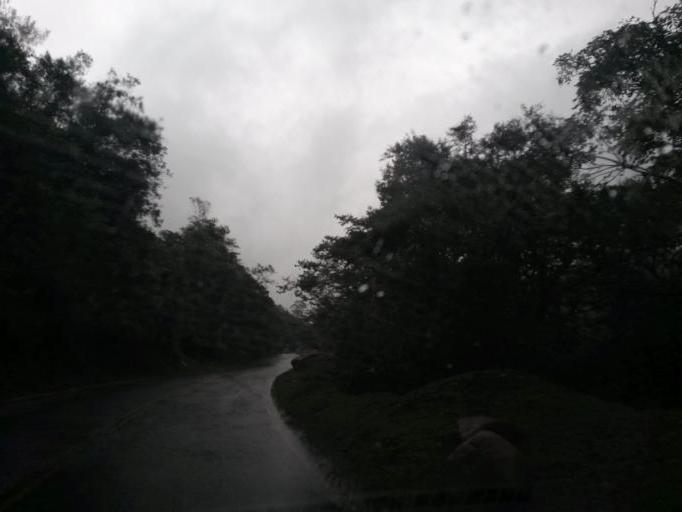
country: CO
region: Cauca
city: Popayan
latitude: 2.3749
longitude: -76.4982
